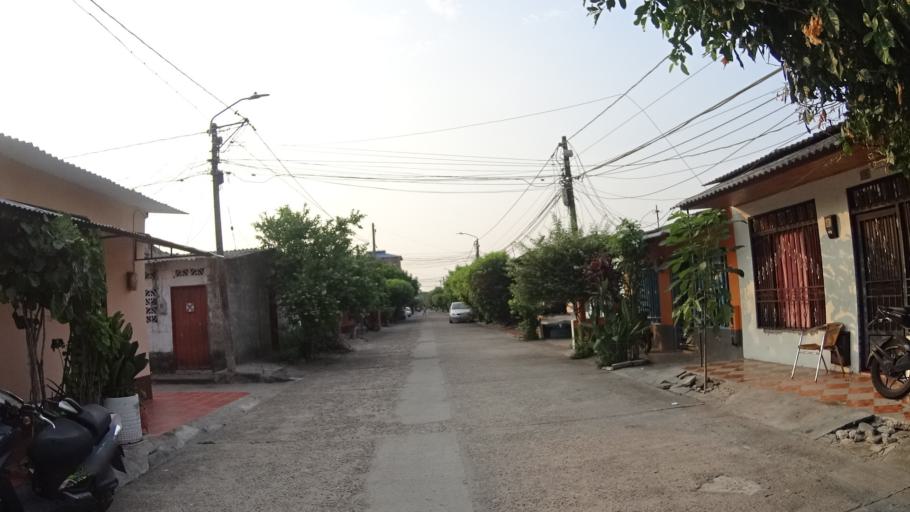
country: CO
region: Caldas
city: La Dorada
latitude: 5.4422
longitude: -74.6577
